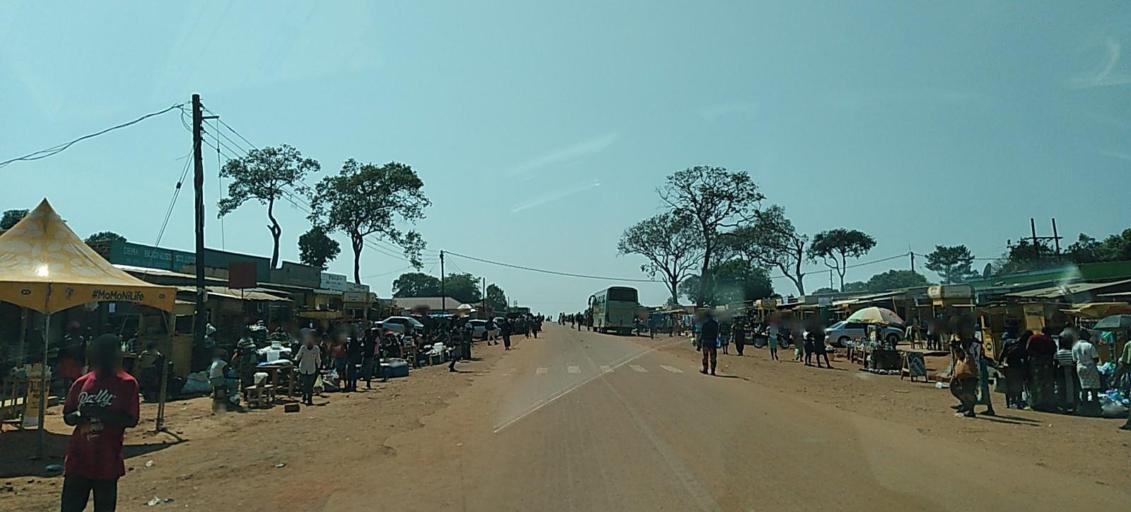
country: ZM
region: North-Western
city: Solwezi
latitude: -12.1091
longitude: 25.4973
